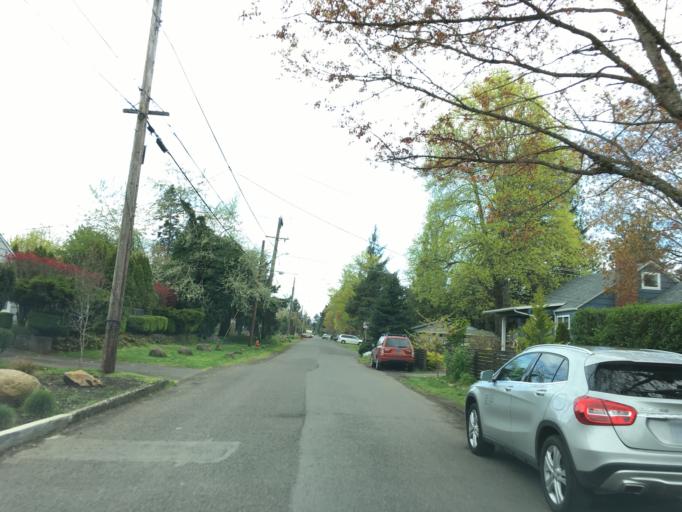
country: US
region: Oregon
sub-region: Multnomah County
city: Lents
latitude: 45.5525
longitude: -122.5985
